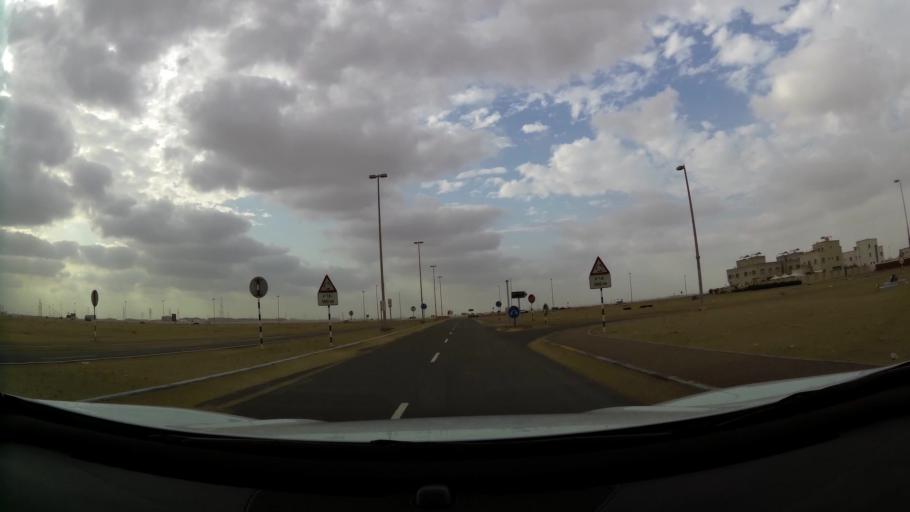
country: AE
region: Abu Dhabi
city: Abu Dhabi
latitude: 24.3476
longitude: 54.6078
